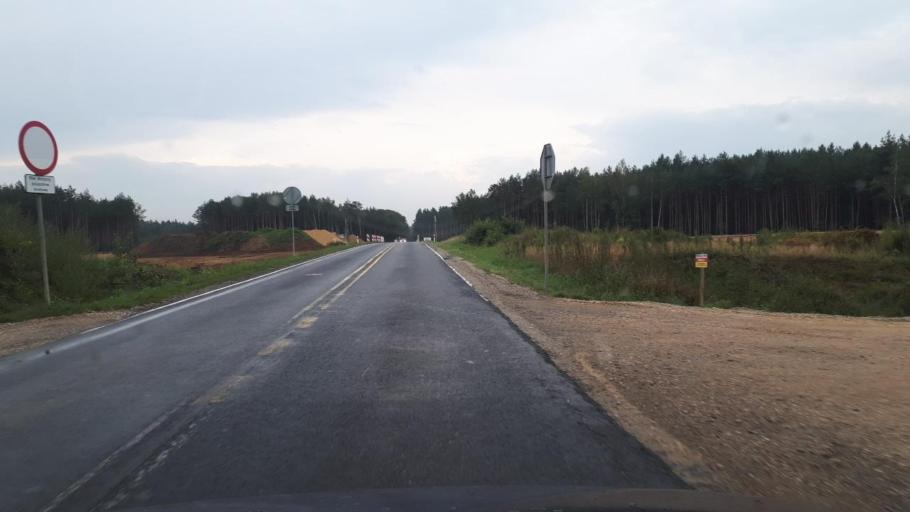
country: PL
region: Silesian Voivodeship
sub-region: Powiat lubliniecki
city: Sierakow Slaski
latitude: 50.8170
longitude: 18.5410
